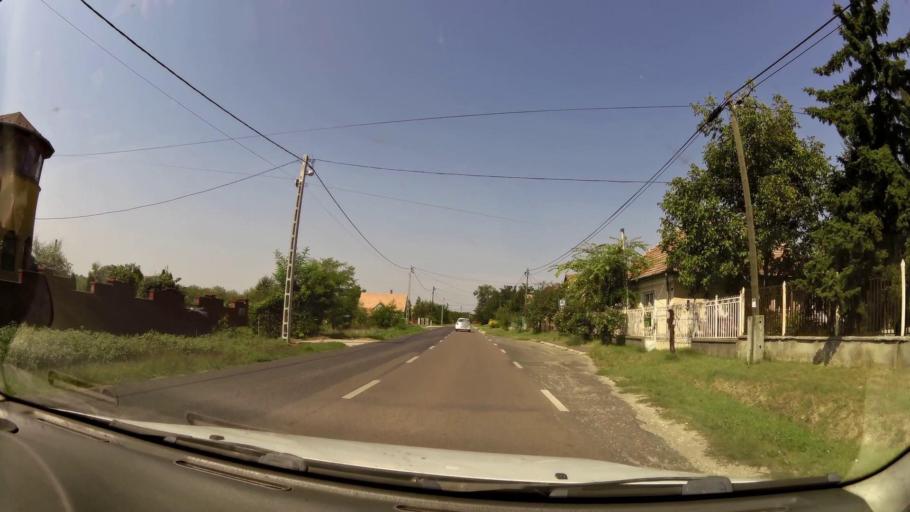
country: HU
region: Pest
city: Tapiobicske
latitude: 47.3692
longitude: 19.6809
